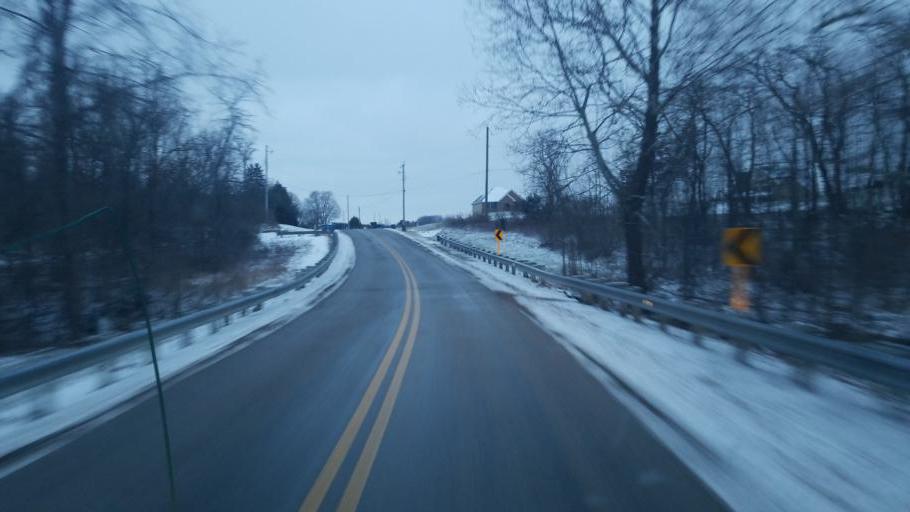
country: US
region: Ohio
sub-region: Delaware County
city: Sunbury
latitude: 40.2077
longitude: -82.8544
